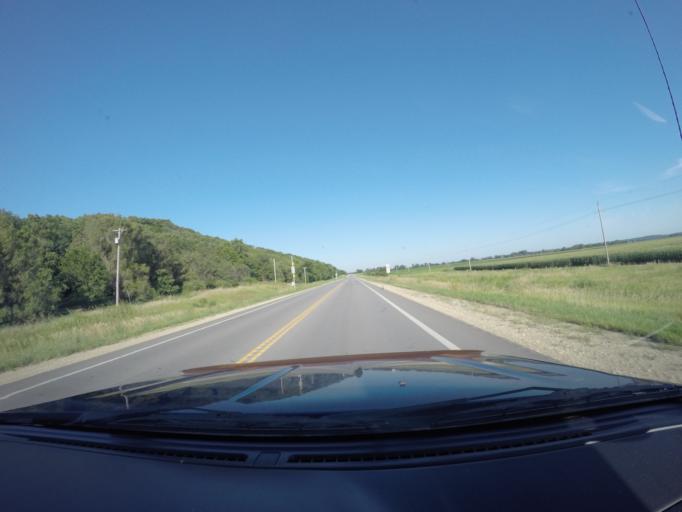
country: US
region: Kansas
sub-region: Jefferson County
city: Oskaloosa
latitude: 39.0780
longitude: -95.3786
